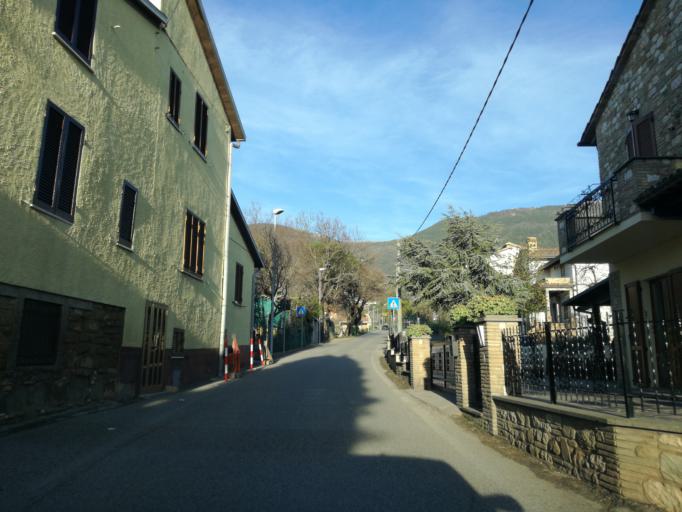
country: IT
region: Umbria
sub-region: Provincia di Perugia
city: Rivotorto
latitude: 43.0443
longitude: 12.6227
